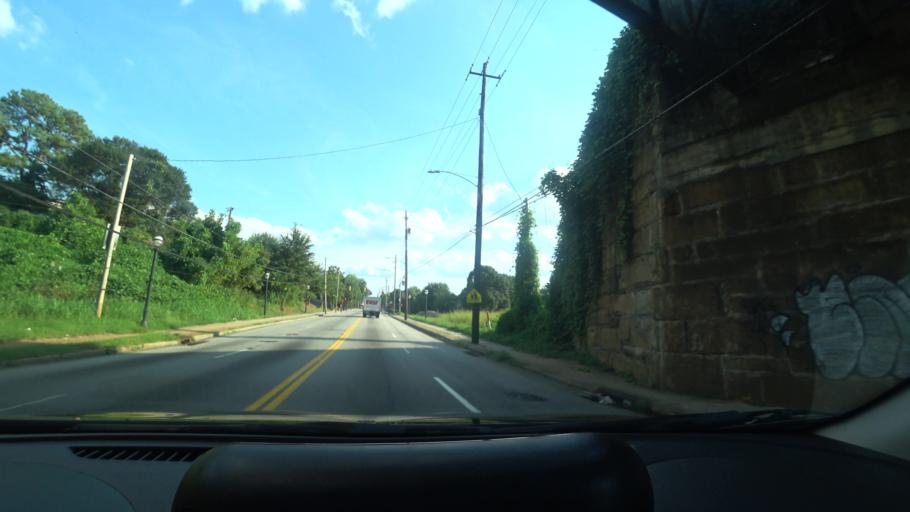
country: US
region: Georgia
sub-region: Fulton County
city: Atlanta
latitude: 33.7196
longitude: -84.3933
